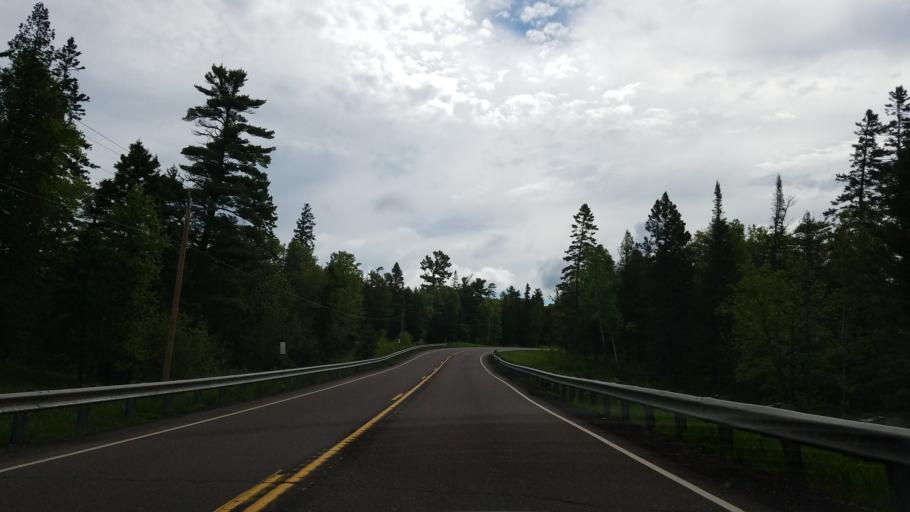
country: US
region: Minnesota
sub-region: Lake County
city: Two Harbors
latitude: 47.0961
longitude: -91.5653
